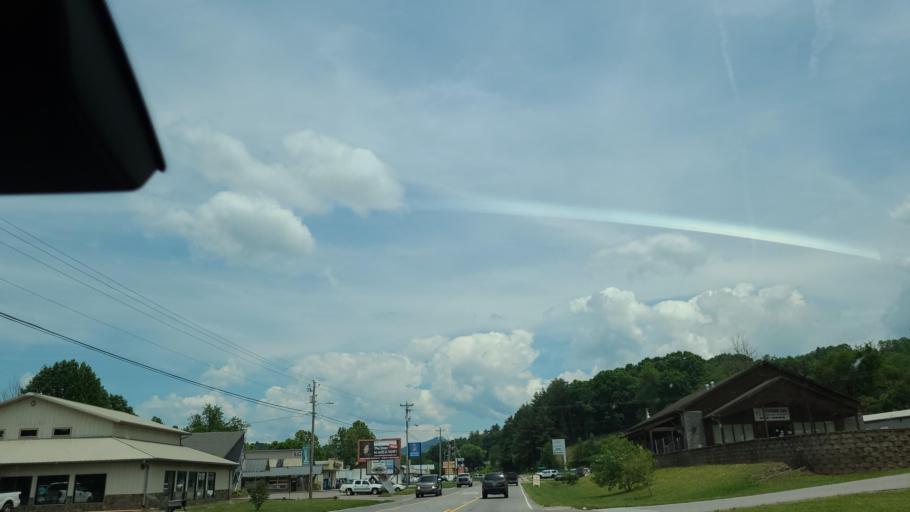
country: US
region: North Carolina
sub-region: Macon County
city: Franklin
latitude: 35.1781
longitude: -83.3674
